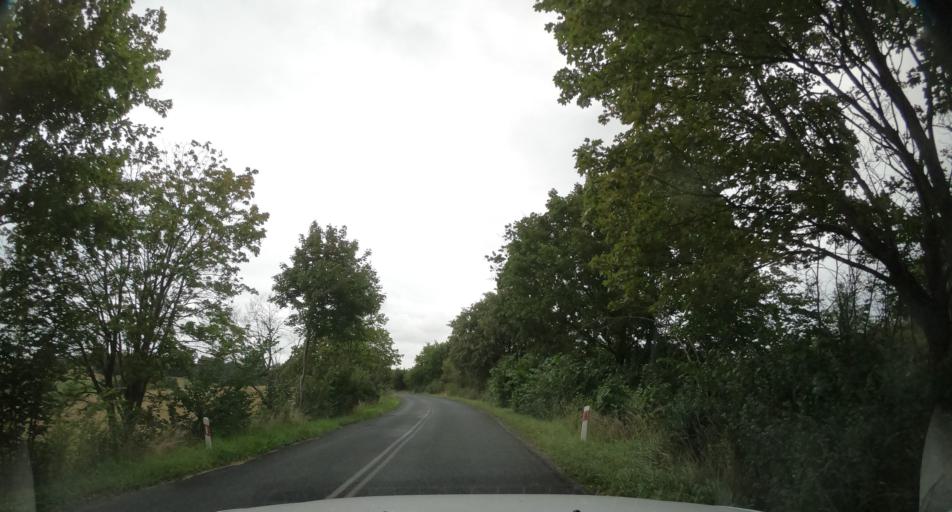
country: PL
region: West Pomeranian Voivodeship
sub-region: Powiat stargardzki
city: Dobrzany
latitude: 53.4188
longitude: 15.4253
